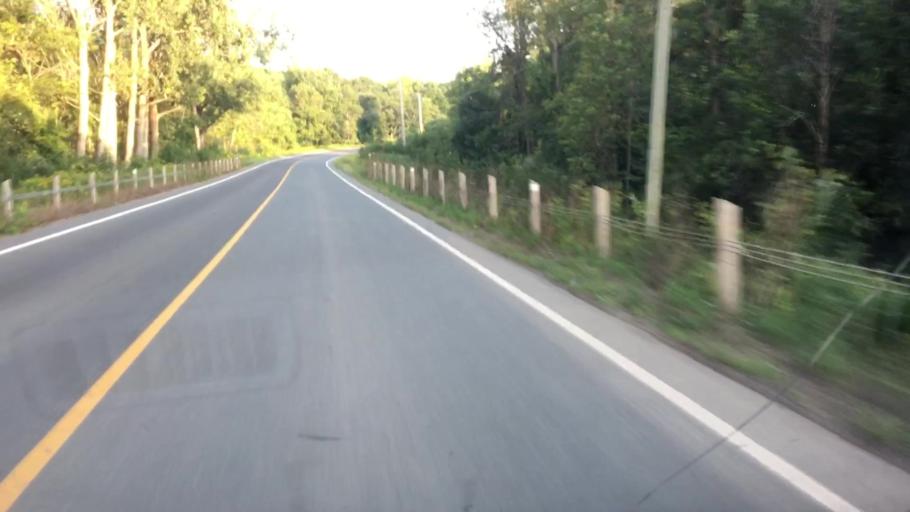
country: CA
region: Ontario
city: Quinte West
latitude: 44.0951
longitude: -77.7341
